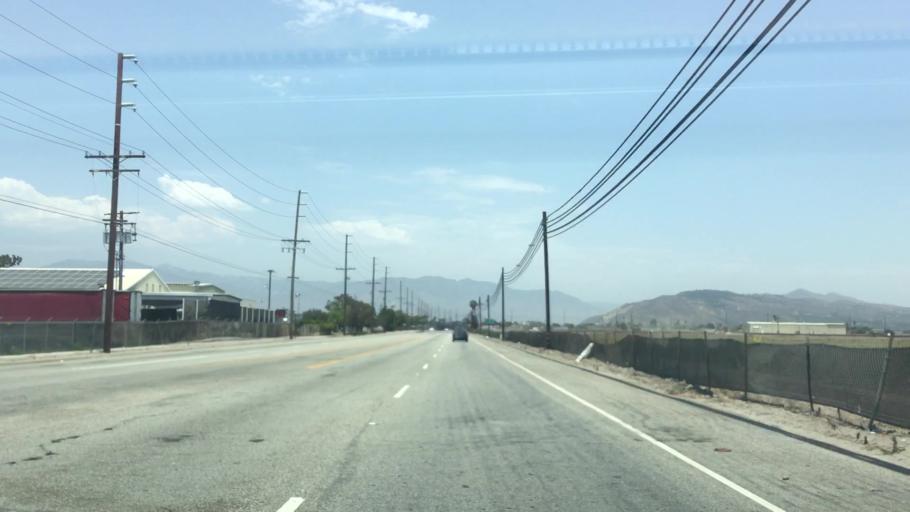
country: US
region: California
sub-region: Ventura County
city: El Rio
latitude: 34.2502
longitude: -119.1593
